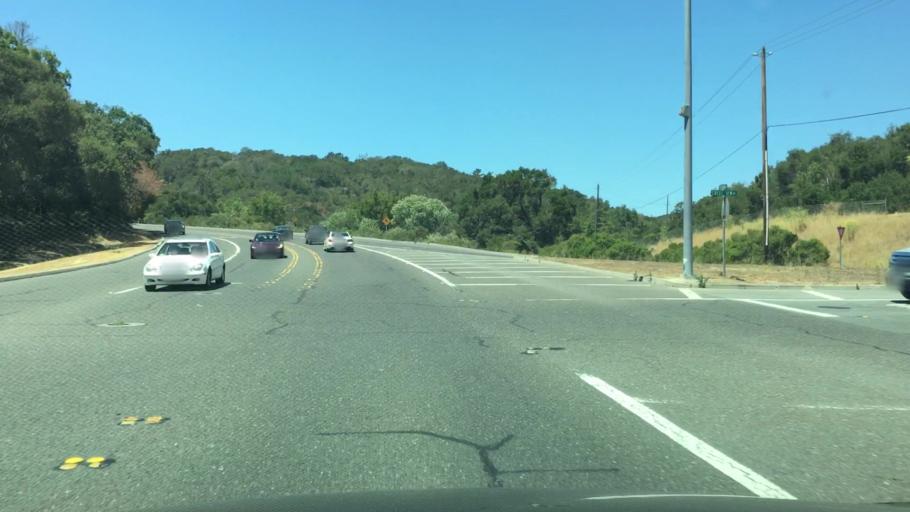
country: US
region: California
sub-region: San Mateo County
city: Emerald Lake Hills
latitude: 37.4746
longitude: -122.2803
